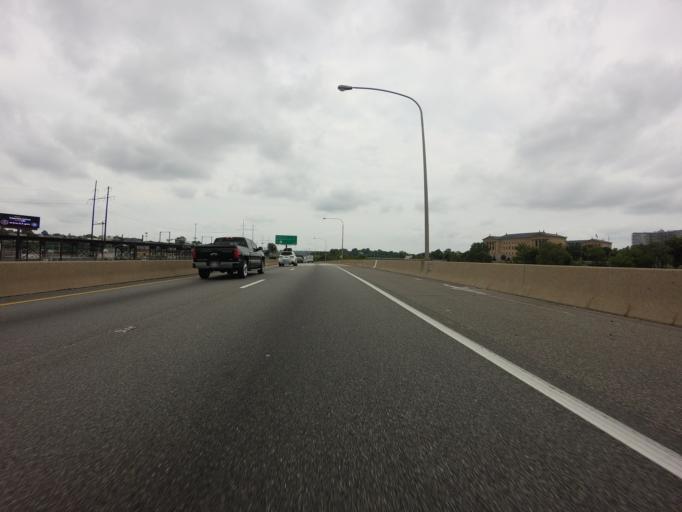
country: US
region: Pennsylvania
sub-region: Philadelphia County
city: Philadelphia
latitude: 39.9615
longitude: -75.1822
